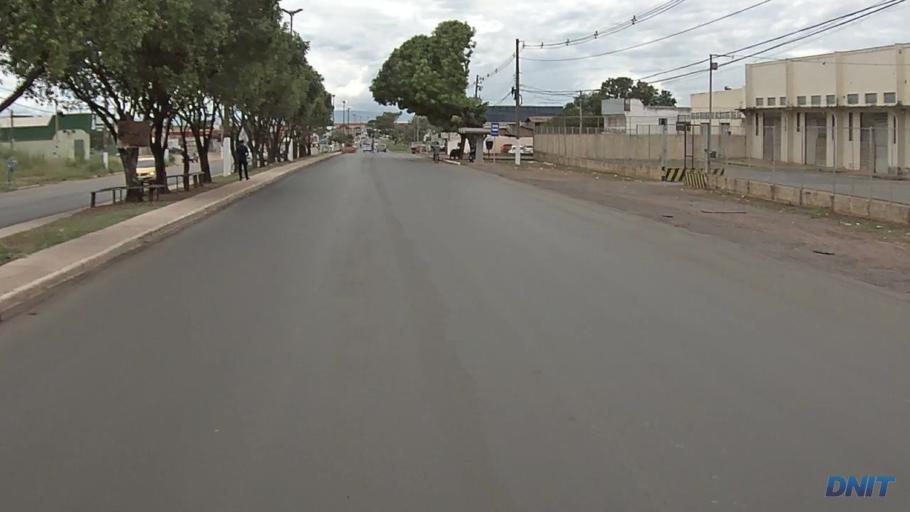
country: BR
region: Mato Grosso
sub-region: Varzea Grande
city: Varzea Grande
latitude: -15.6446
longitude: -56.1835
